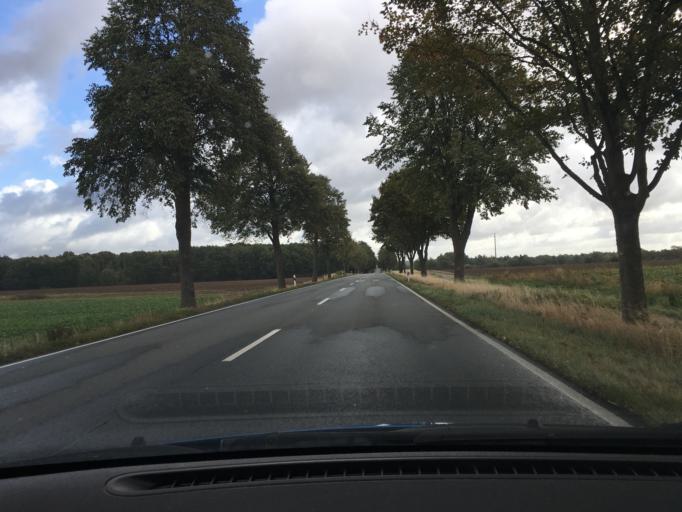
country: DE
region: Lower Saxony
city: Suhlendorf
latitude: 52.9353
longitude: 10.7552
